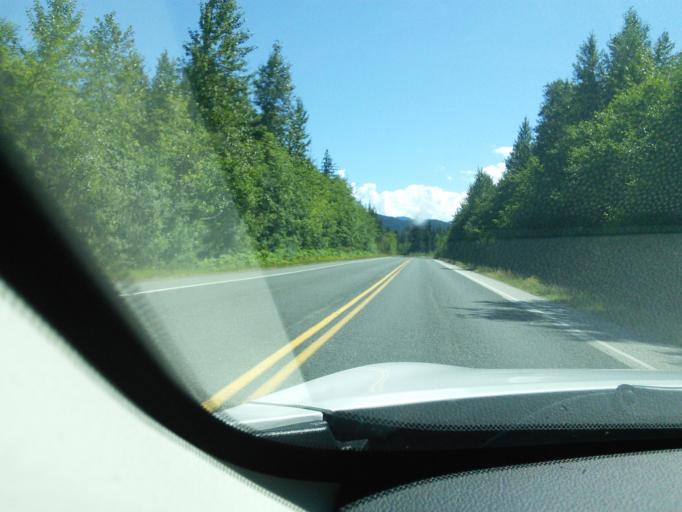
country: CA
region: British Columbia
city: Campbell River
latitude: 50.3588
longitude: -125.9133
